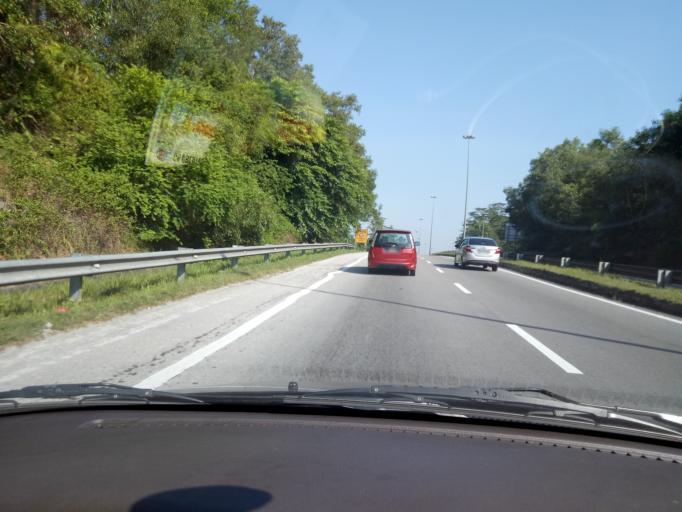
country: MY
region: Selangor
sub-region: Hulu Langat
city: Semenyih
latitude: 2.9861
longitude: 101.8264
